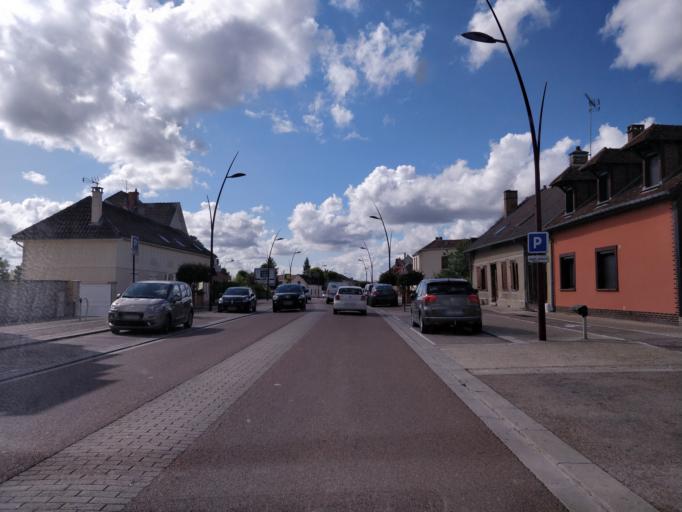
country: FR
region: Champagne-Ardenne
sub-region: Departement de l'Aube
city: Saint-Parres-aux-Tertres
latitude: 48.2988
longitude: 4.1151
